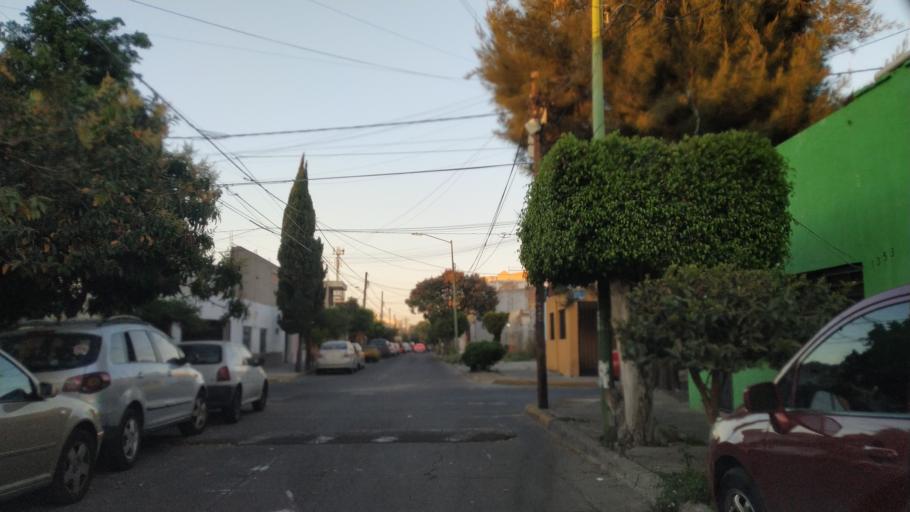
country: MX
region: Jalisco
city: Tlaquepaque
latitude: 20.6554
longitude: -103.3350
